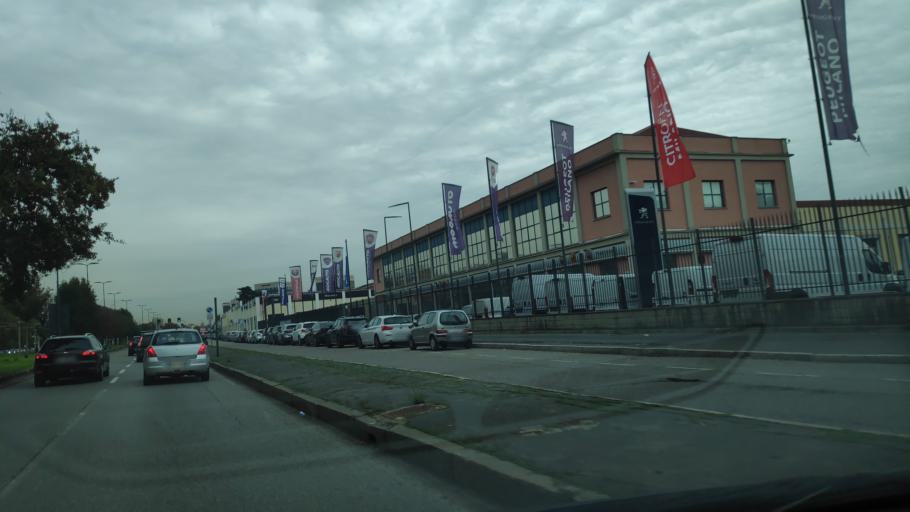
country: IT
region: Lombardy
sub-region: Citta metropolitana di Milano
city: Rozzano
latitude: 45.4114
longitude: 9.1749
